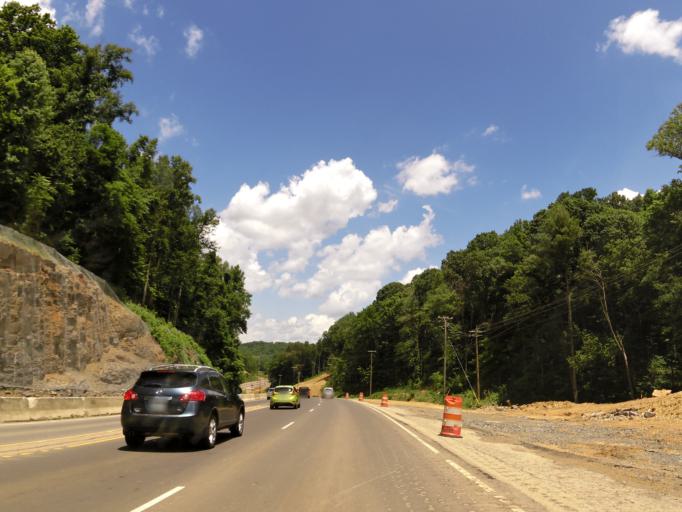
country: US
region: Tennessee
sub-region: Union County
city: Condon
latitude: 36.1508
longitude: -83.9122
